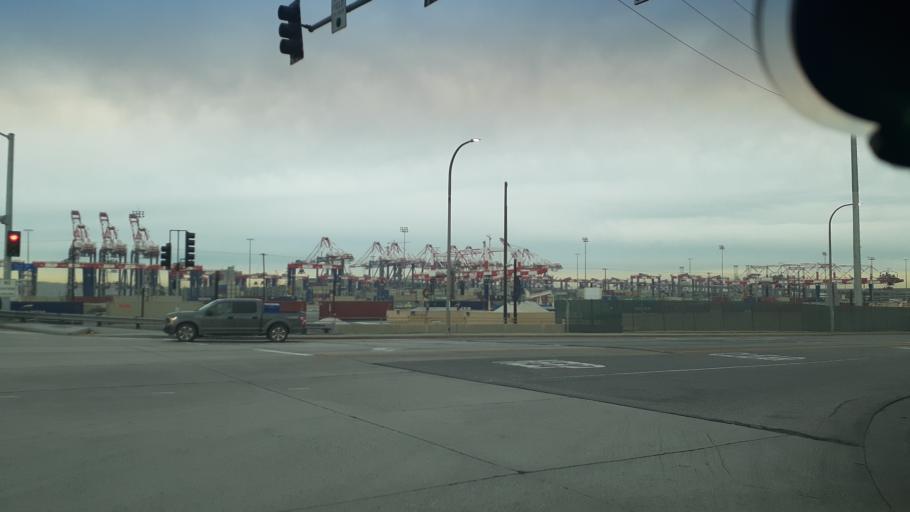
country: US
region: California
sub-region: Los Angeles County
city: Long Beach
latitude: 33.7560
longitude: -118.2039
